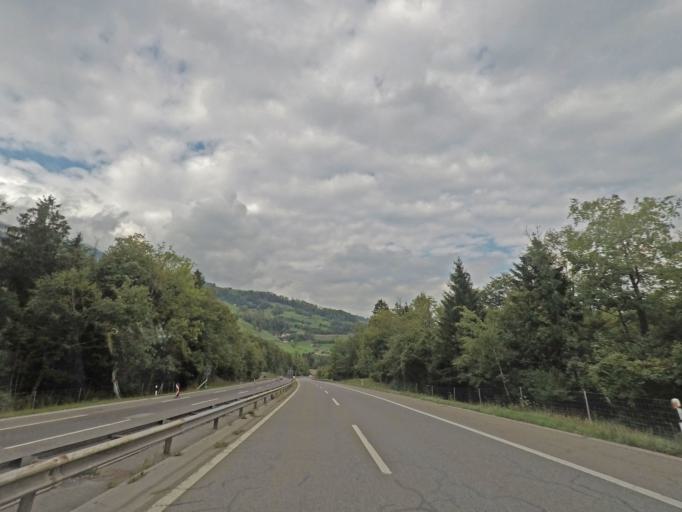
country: CH
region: Schwyz
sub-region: Bezirk Schwyz
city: Goldau
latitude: 47.0467
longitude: 8.5624
